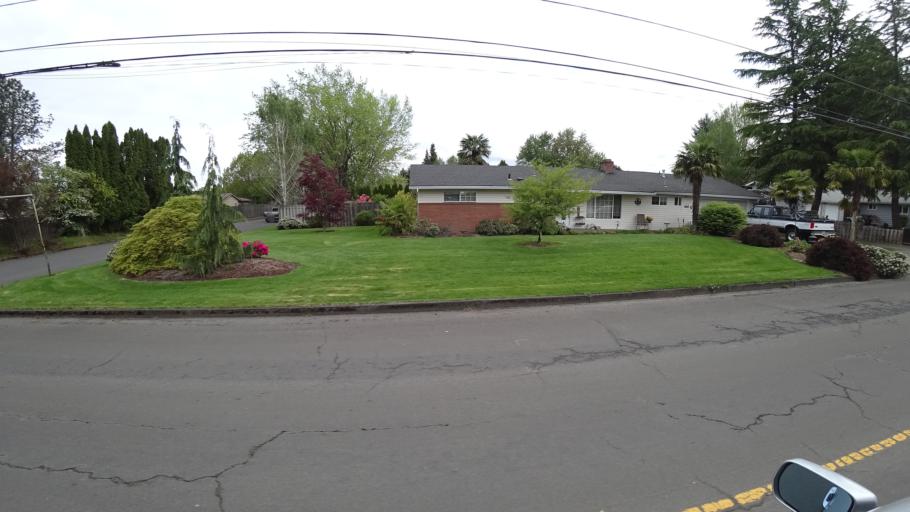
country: US
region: Oregon
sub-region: Washington County
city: Hillsboro
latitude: 45.5327
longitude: -122.9754
